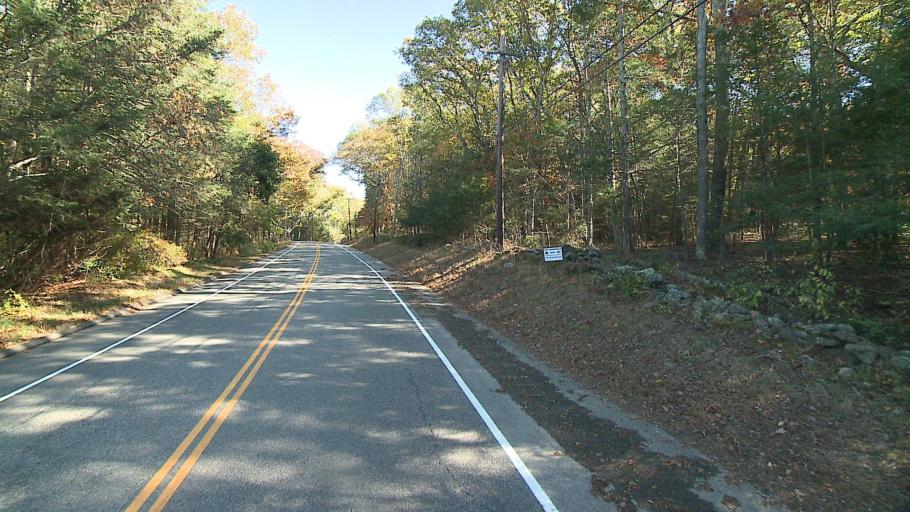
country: US
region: Connecticut
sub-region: Tolland County
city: Storrs
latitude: 41.8210
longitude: -72.2842
